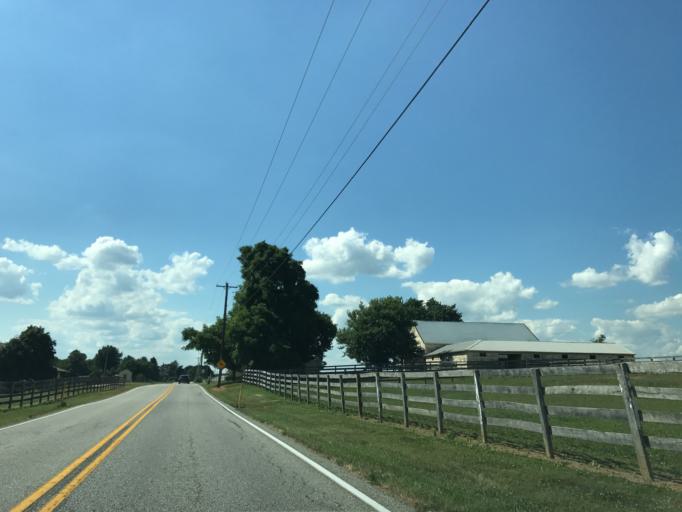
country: US
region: Pennsylvania
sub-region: Adams County
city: McSherrystown
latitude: 39.7839
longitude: -77.0315
